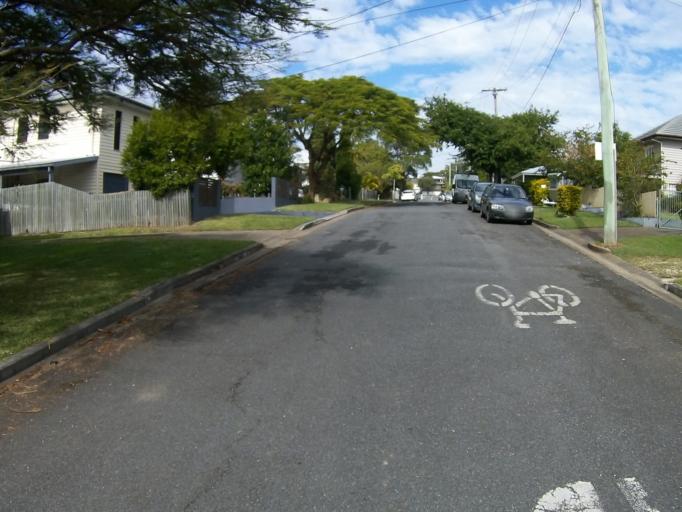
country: AU
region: Queensland
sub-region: Brisbane
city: Greenslopes
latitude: -27.5170
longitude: 153.0474
